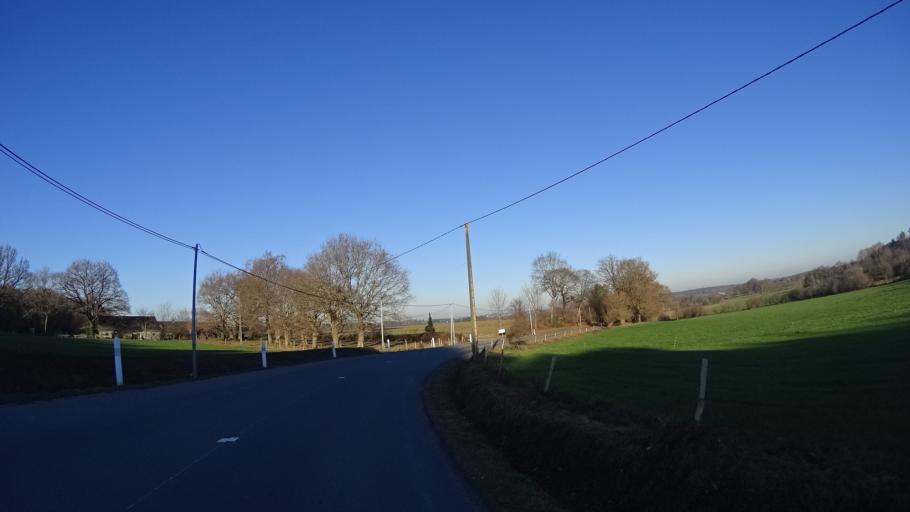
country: FR
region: Brittany
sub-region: Departement du Morbihan
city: Allaire
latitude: 47.6639
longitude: -2.1747
